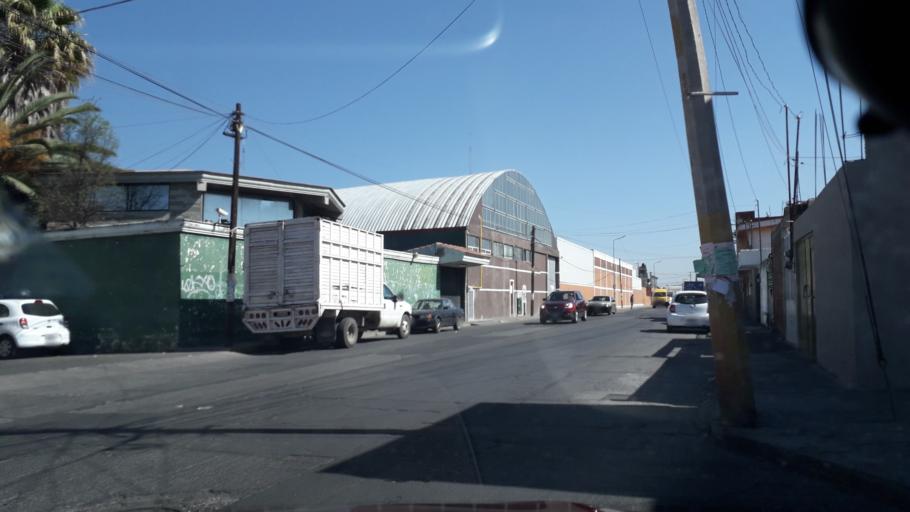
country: MX
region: Puebla
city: Puebla
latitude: 19.0791
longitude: -98.2116
